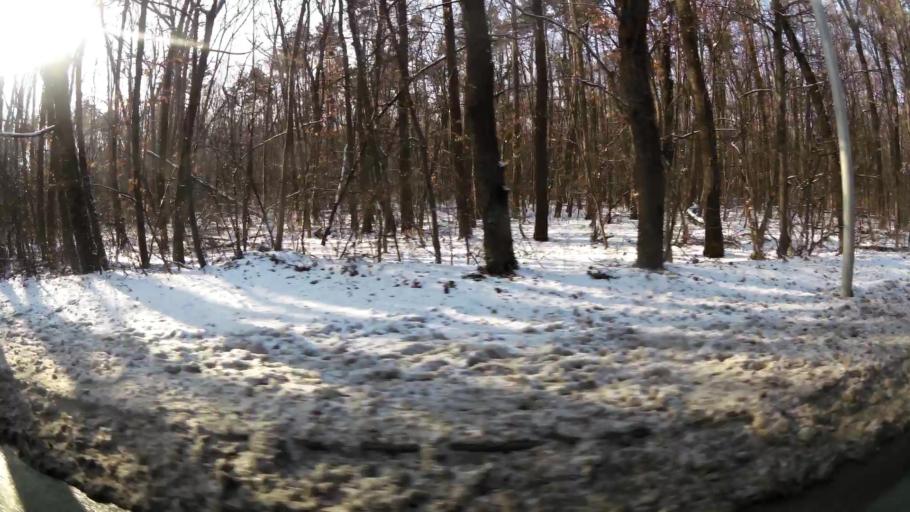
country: BG
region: Sofia-Capital
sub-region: Stolichna Obshtina
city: Sofia
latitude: 42.6698
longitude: 23.3378
